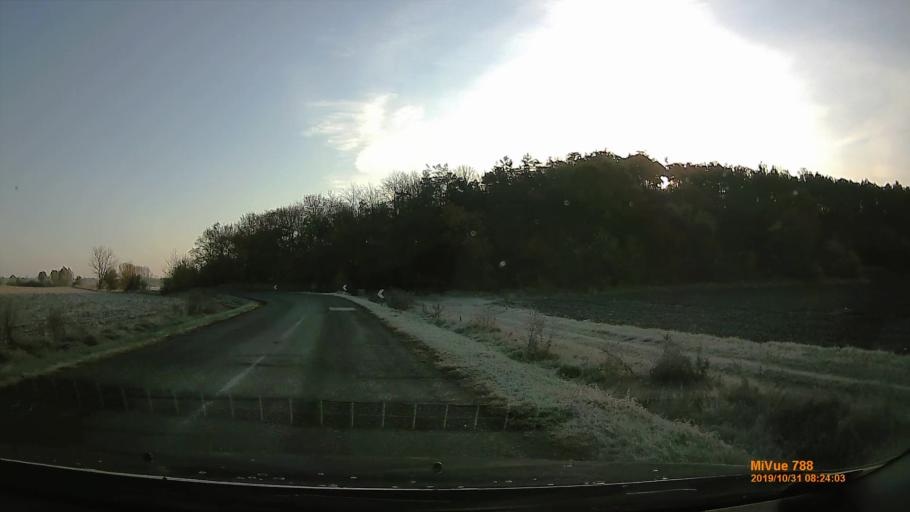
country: HU
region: Pest
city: Pand
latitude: 47.3679
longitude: 19.6539
